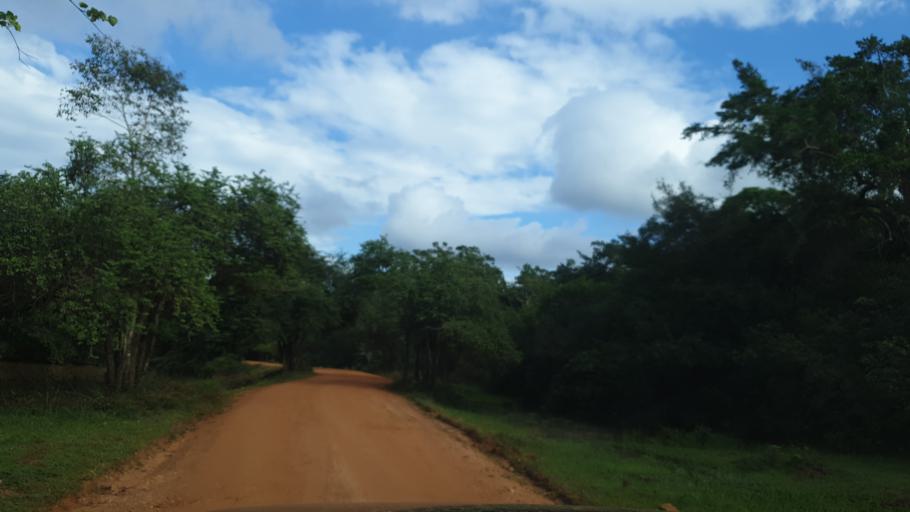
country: LK
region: North Central
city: Anuradhapura
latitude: 8.3635
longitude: 80.0999
